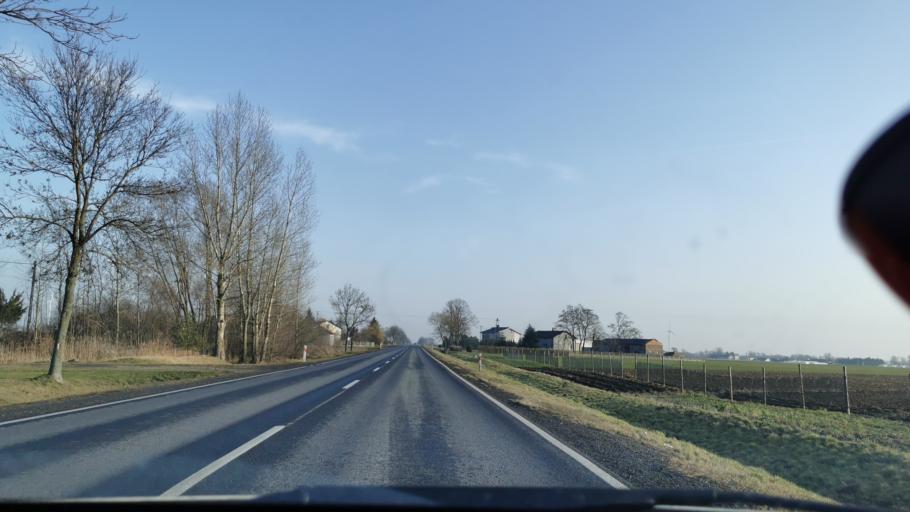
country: PL
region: Lodz Voivodeship
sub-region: Powiat sieradzki
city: Blaszki
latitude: 51.6733
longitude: 18.3647
